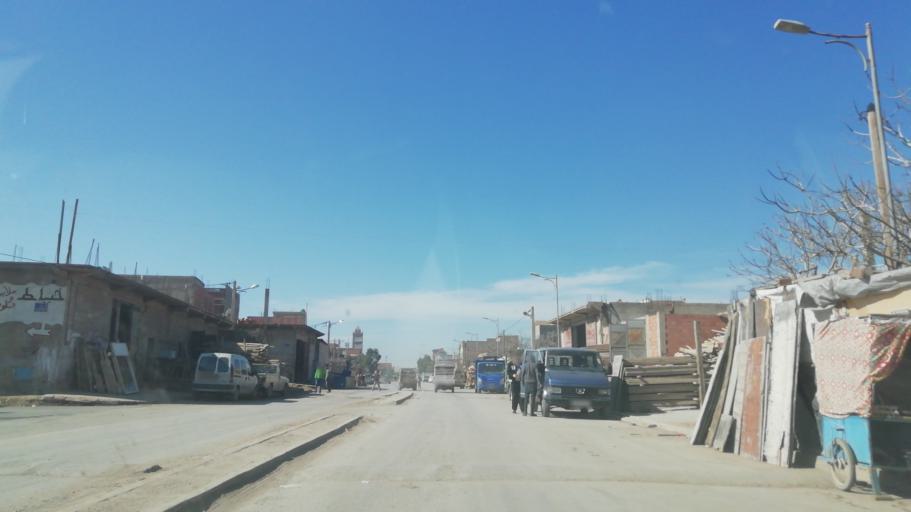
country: DZ
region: Oran
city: Es Senia
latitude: 35.6460
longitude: -0.5751
